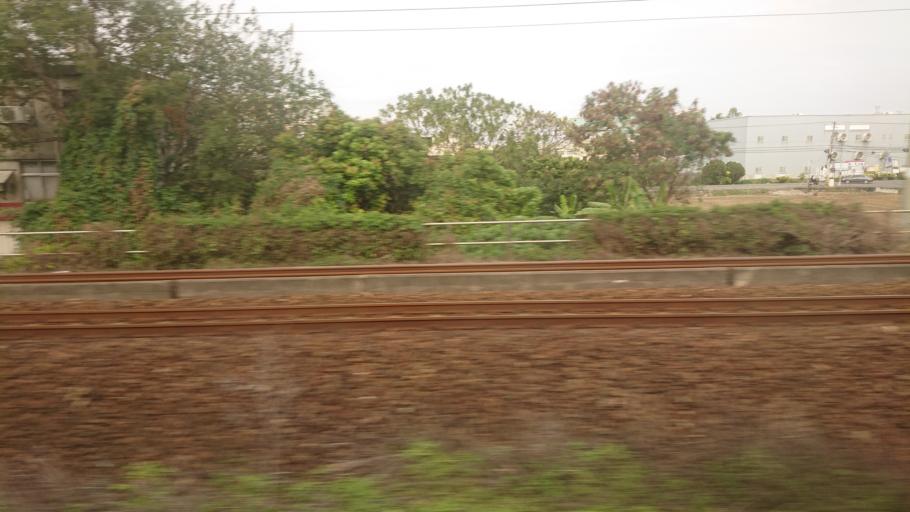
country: TW
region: Taiwan
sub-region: Changhua
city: Chang-hua
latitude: 24.0988
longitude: 120.5727
